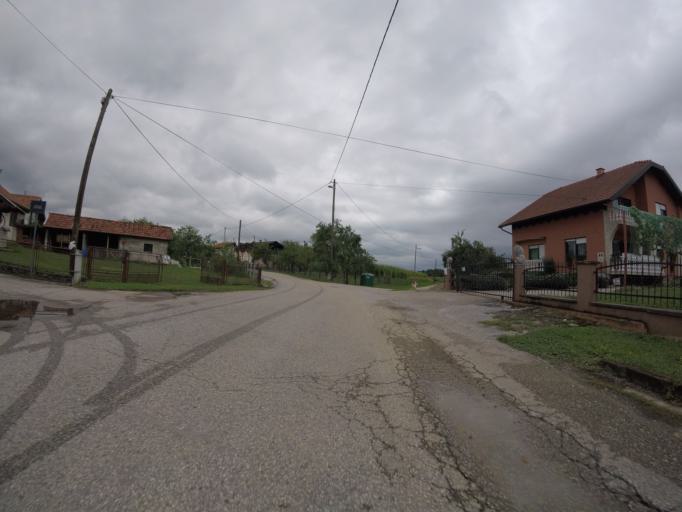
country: HR
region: Zagrebacka
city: Mraclin
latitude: 45.6035
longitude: 16.0835
